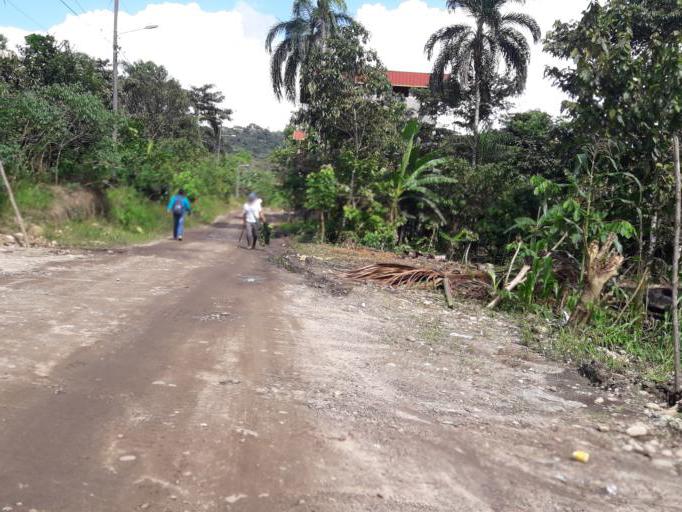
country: EC
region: Napo
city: Tena
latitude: -0.9558
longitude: -77.8207
